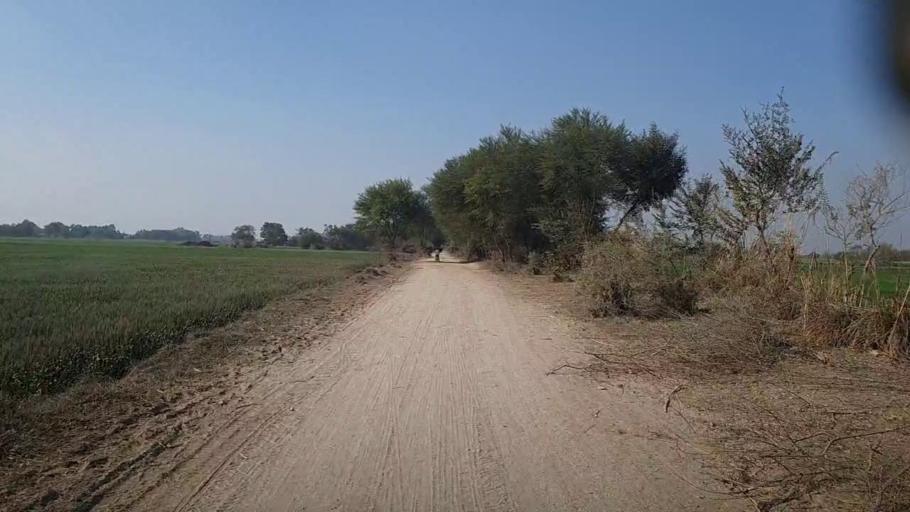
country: PK
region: Sindh
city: Mirpur Mathelo
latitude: 27.8955
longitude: 69.6539
